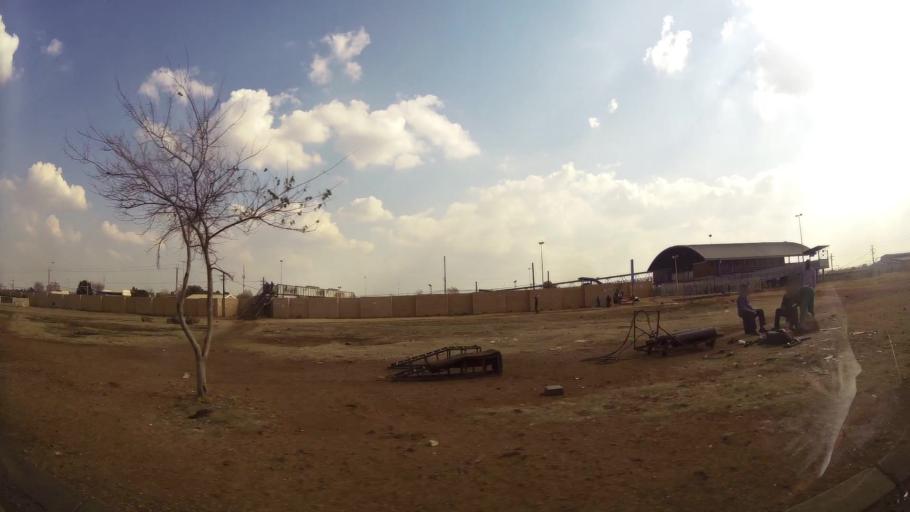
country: ZA
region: Gauteng
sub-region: Ekurhuleni Metropolitan Municipality
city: Germiston
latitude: -26.3412
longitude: 28.1532
